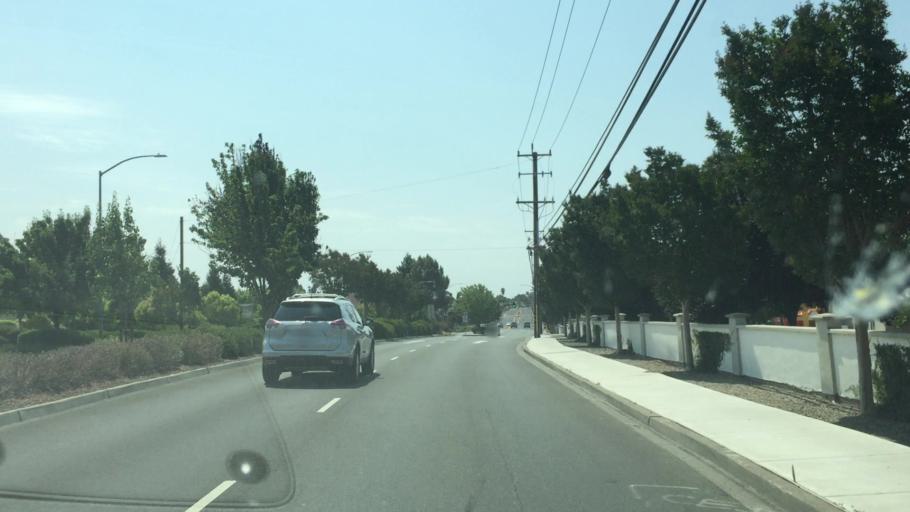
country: US
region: California
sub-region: Napa County
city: American Canyon
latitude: 38.1567
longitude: -122.2387
